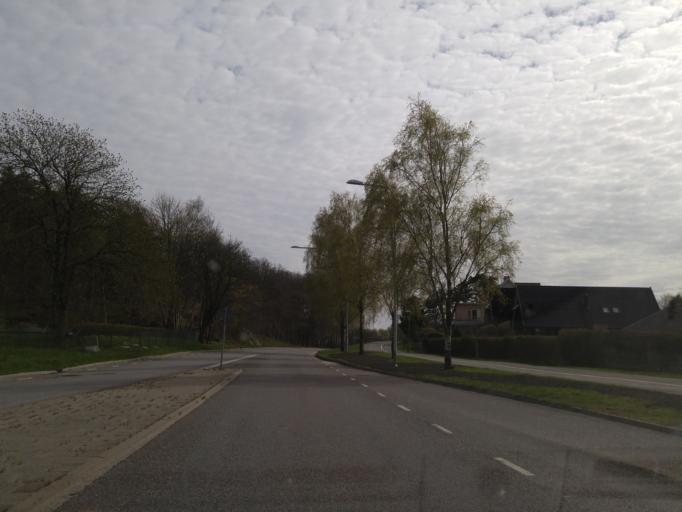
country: SE
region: Vaestra Goetaland
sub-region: Goteborg
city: Majorna
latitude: 57.6594
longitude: 11.8720
